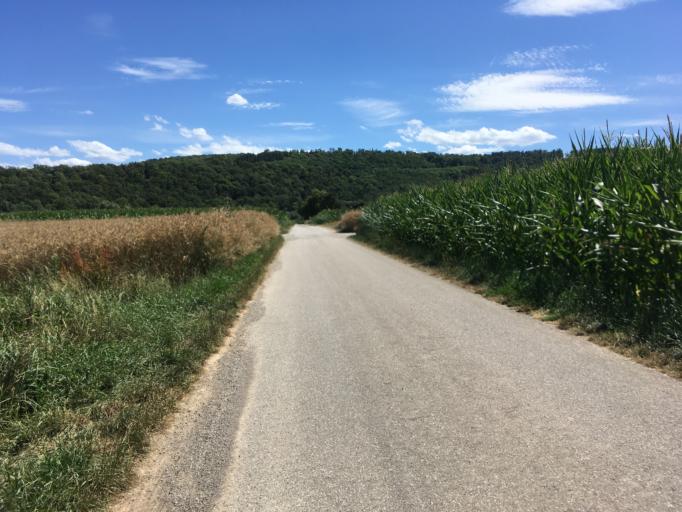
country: DE
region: Baden-Wuerttemberg
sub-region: Karlsruhe Region
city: Illingen
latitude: 48.9353
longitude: 8.8928
